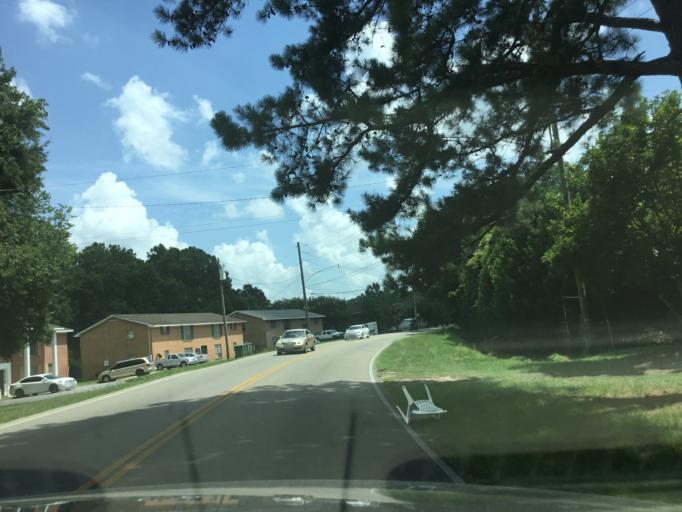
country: US
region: Alabama
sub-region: Montgomery County
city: Montgomery
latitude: 32.3998
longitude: -86.2594
